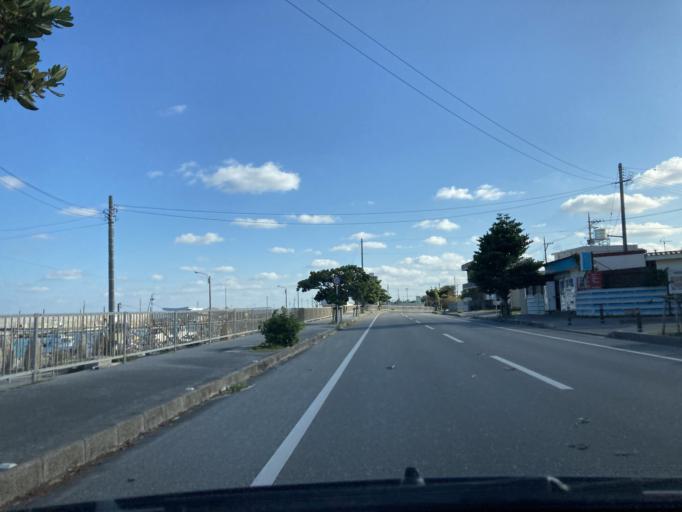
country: JP
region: Okinawa
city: Katsuren-haebaru
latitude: 26.3104
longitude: 127.9201
